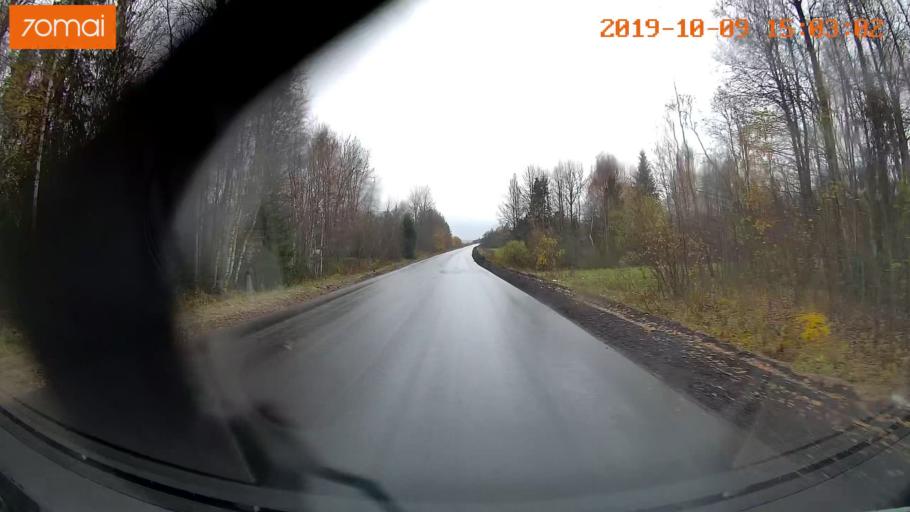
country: RU
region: Kostroma
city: Chistyye Bory
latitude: 58.2770
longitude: 41.6764
